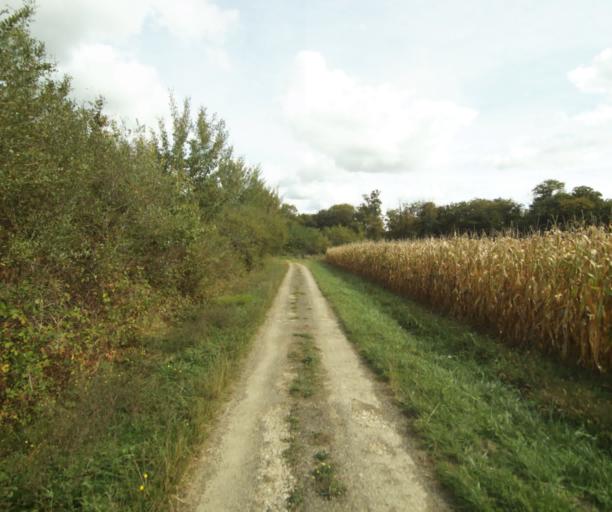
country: FR
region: Midi-Pyrenees
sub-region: Departement du Gers
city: Eauze
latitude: 43.8399
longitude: 0.1016
